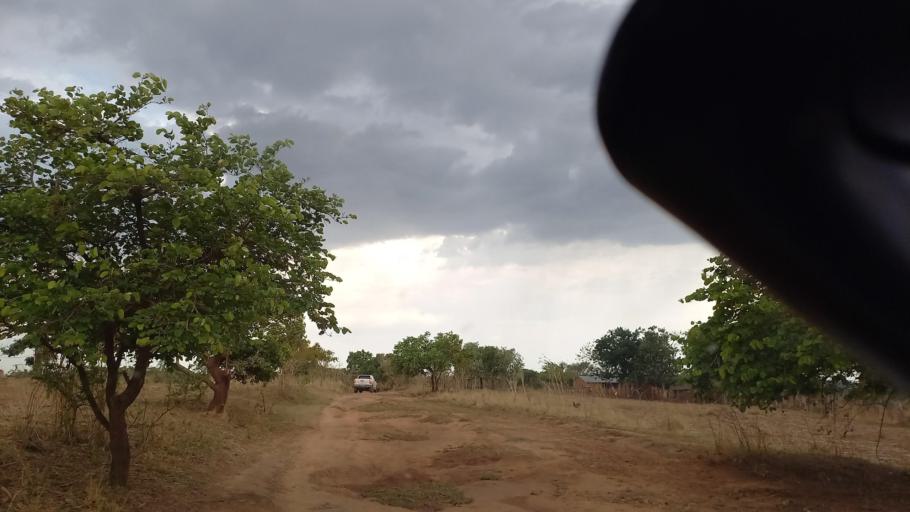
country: ZM
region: Lusaka
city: Kafue
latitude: -16.1284
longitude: 28.0604
